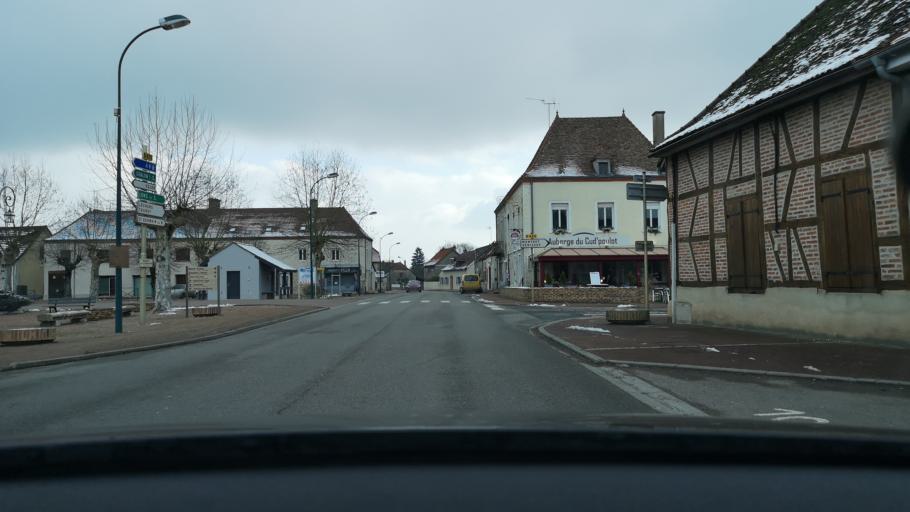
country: FR
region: Bourgogne
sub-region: Departement de Saone-et-Loire
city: Saint-Martin-en-Bresse
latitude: 46.7409
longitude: 5.0927
